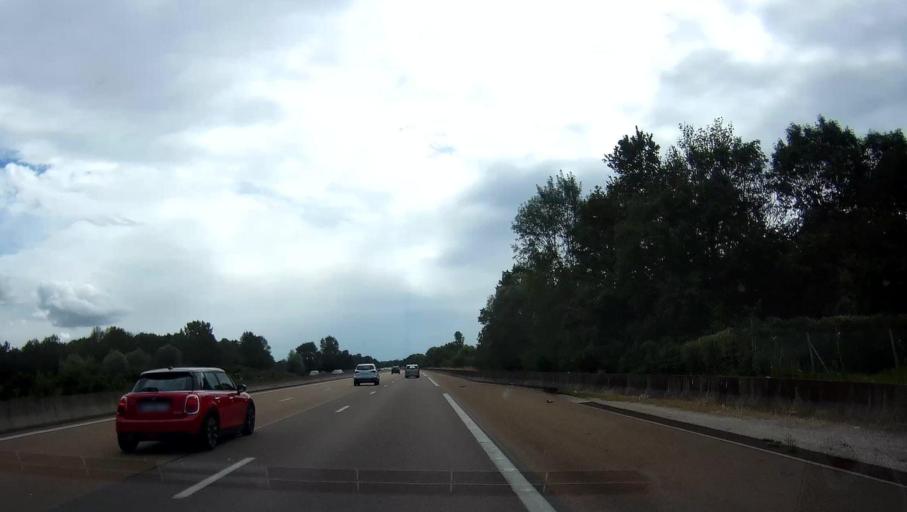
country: FR
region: Bourgogne
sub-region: Departement de la Cote-d'Or
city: Saint-Julien
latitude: 47.3840
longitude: 5.1701
